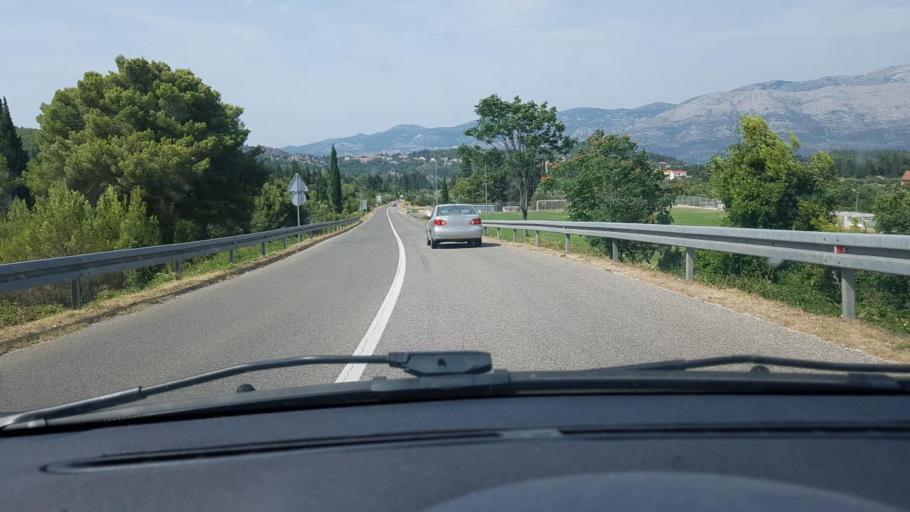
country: HR
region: Dubrovacko-Neretvanska
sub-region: Grad Korcula
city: Zrnovo
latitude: 42.9359
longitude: 17.1045
